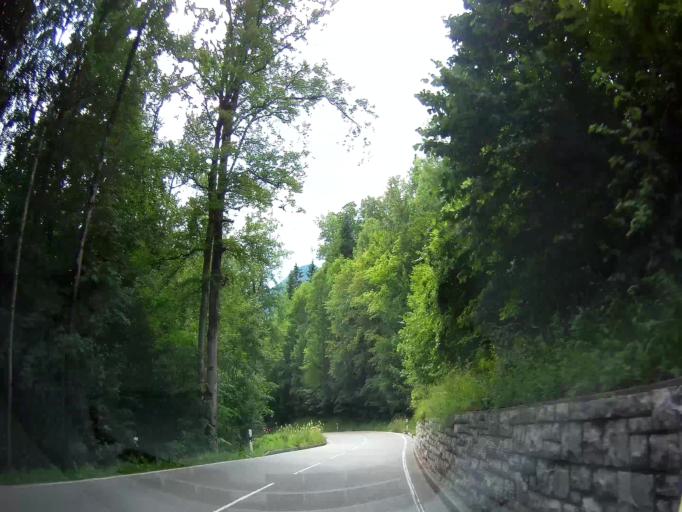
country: DE
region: Bavaria
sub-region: Upper Bavaria
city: Marktschellenberg
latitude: 47.6517
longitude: 13.0561
